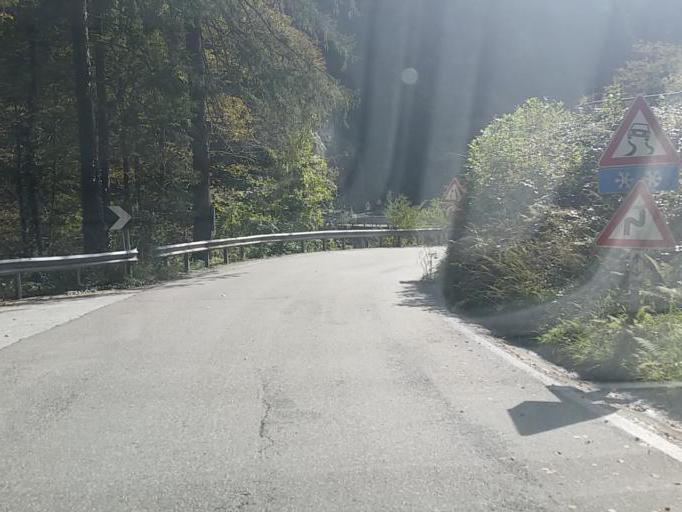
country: IT
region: Piedmont
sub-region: Provincia Verbano-Cusio-Ossola
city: Falmenta
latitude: 46.0758
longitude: 8.6014
